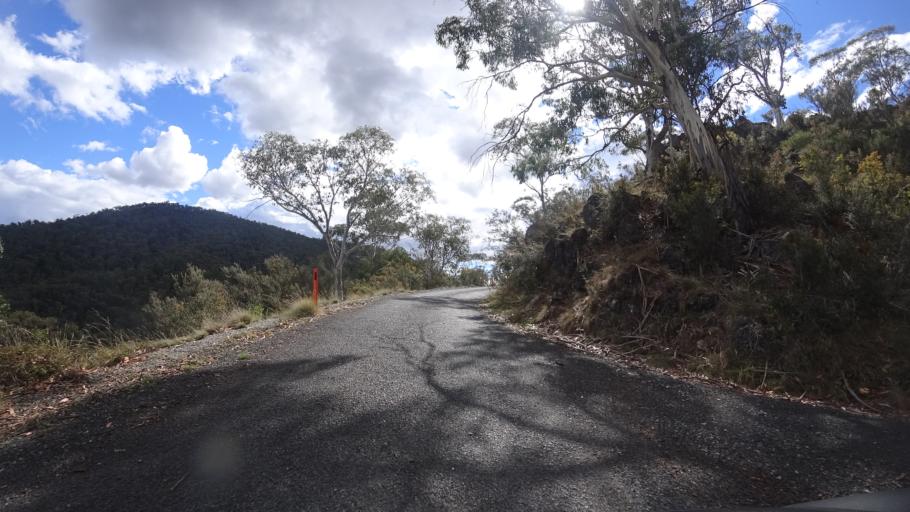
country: AU
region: New South Wales
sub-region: Tumut Shire
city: Tumut
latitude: -35.7235
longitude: 148.4875
